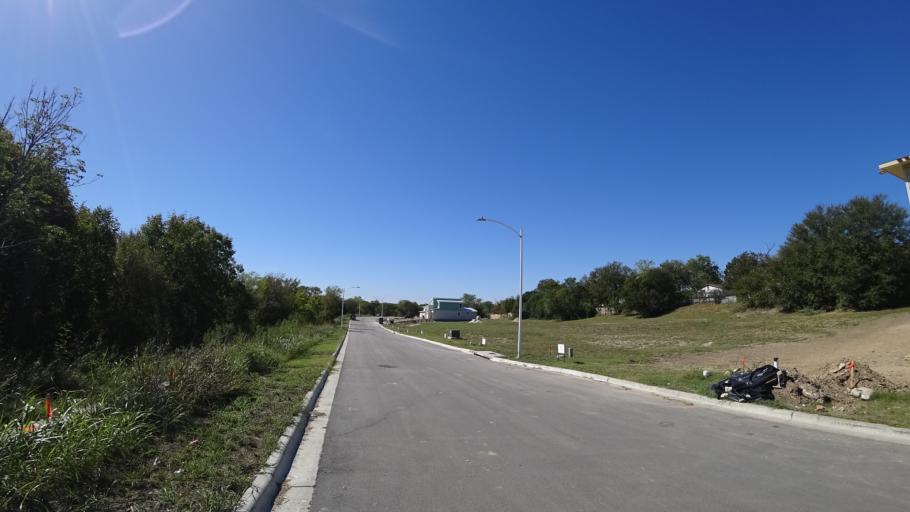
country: US
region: Texas
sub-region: Travis County
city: Austin
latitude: 30.2825
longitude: -97.6787
